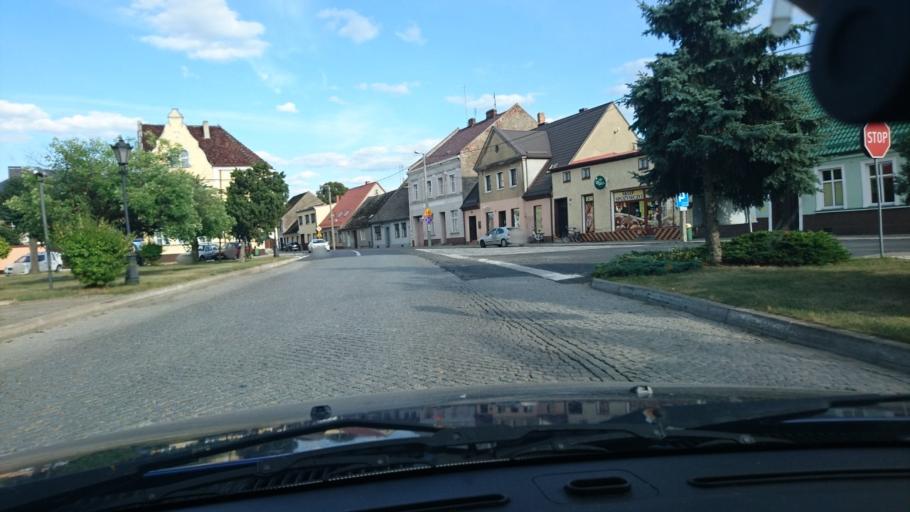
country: PL
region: Greater Poland Voivodeship
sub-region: Powiat krotoszynski
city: Sulmierzyce
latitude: 51.6062
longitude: 17.5278
